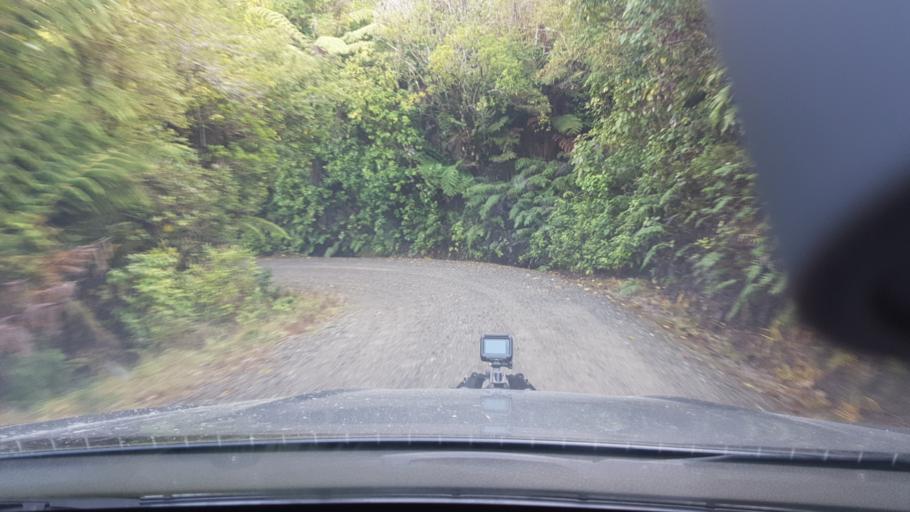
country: NZ
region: Marlborough
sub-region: Marlborough District
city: Picton
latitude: -41.2215
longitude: 173.9655
